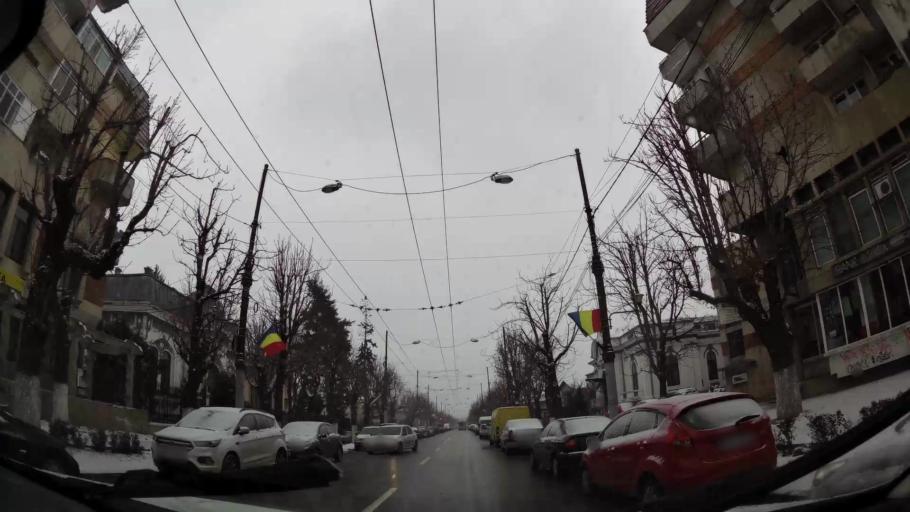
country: RO
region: Dambovita
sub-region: Municipiul Targoviste
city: Targoviste
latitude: 44.9243
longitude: 25.4580
